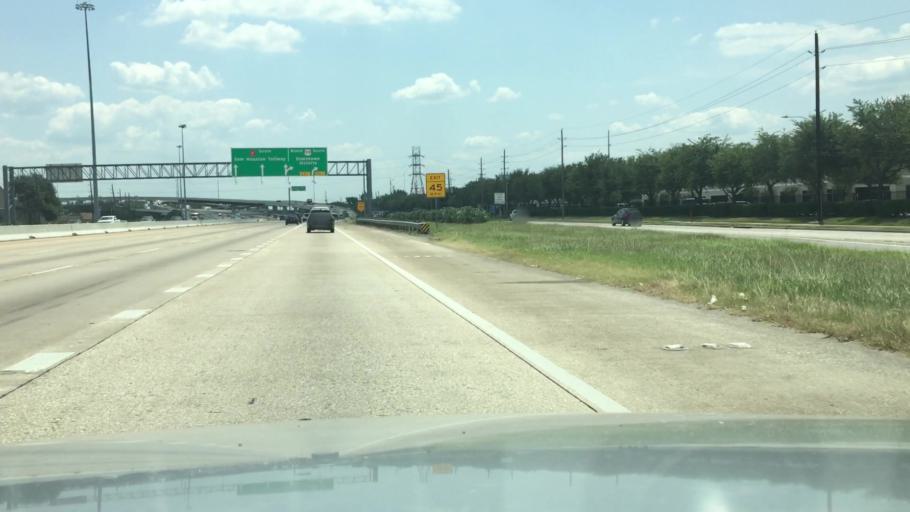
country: US
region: Texas
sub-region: Fort Bend County
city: Meadows Place
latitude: 29.6706
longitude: -95.5605
